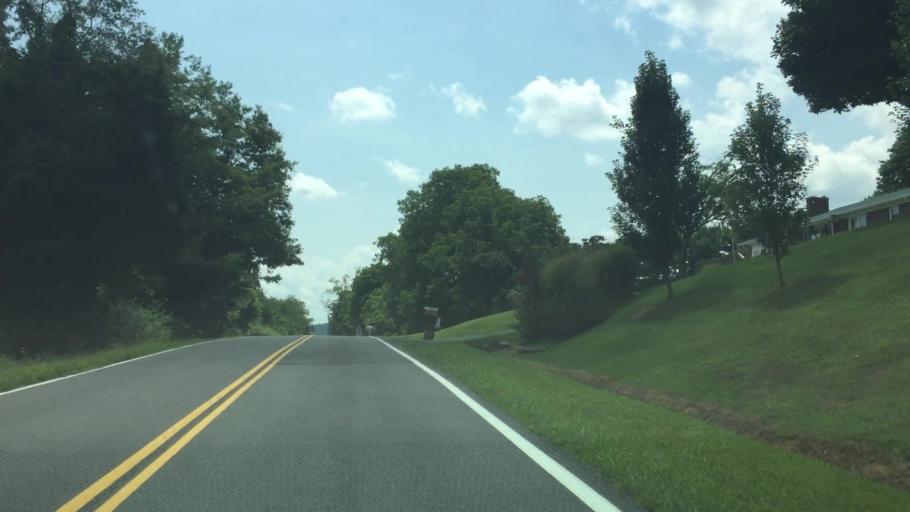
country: US
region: Virginia
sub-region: Pulaski County
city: Pulaski
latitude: 36.9830
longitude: -80.8285
